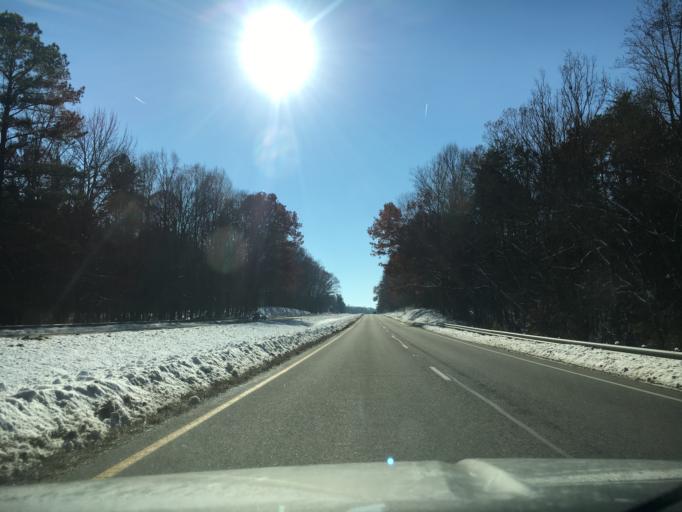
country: US
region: Virginia
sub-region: Nottoway County
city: Crewe
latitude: 37.2902
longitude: -78.1045
